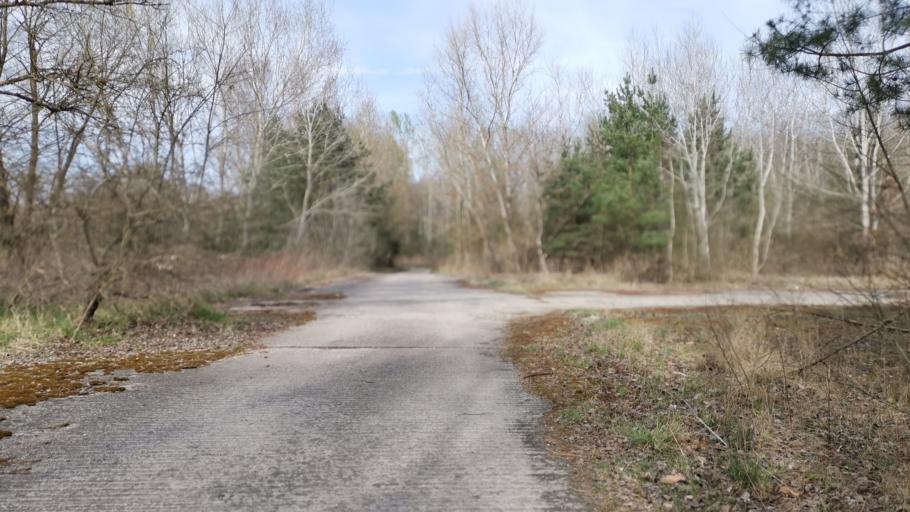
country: SK
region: Trnavsky
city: Gbely
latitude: 48.6692
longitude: 17.0532
